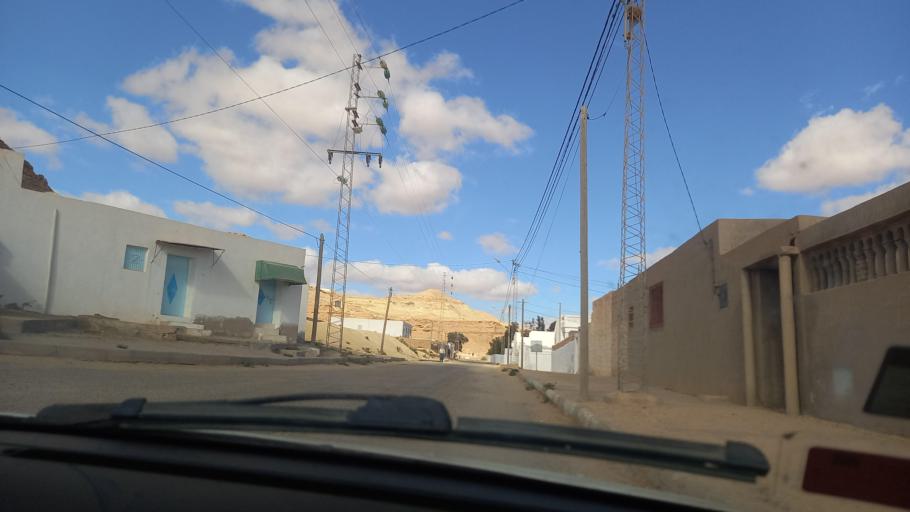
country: TN
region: Tataouine
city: Tataouine
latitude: 32.9826
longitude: 10.2634
